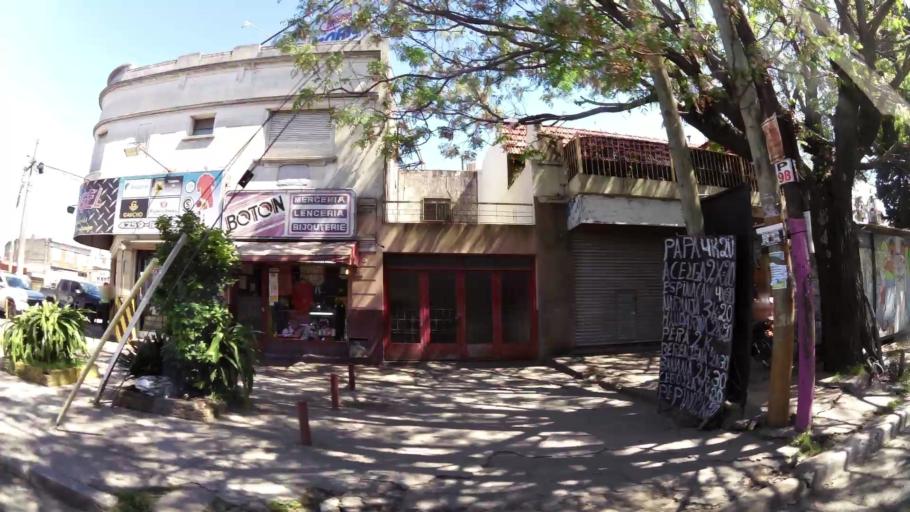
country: AR
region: Buenos Aires
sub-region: Partido de Quilmes
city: Quilmes
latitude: -34.7162
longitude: -58.3047
